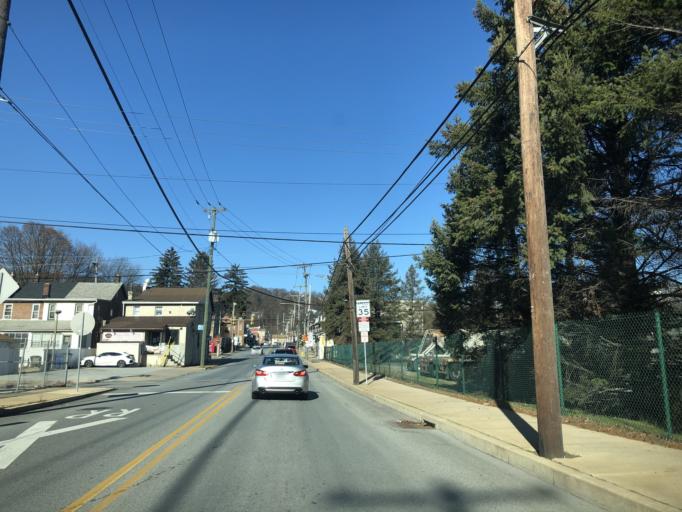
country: US
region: Pennsylvania
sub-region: Chester County
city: Coatesville
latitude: 39.9774
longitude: -75.8294
